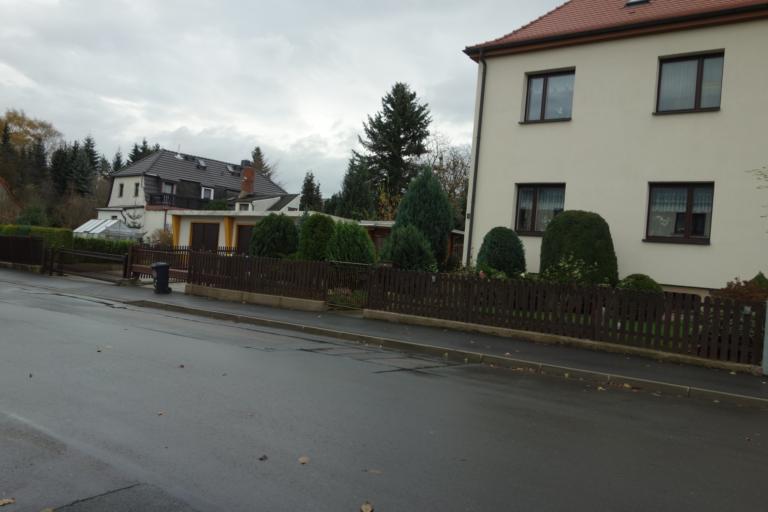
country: DE
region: Saxony
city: Freiberg
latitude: 50.9030
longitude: 13.3511
